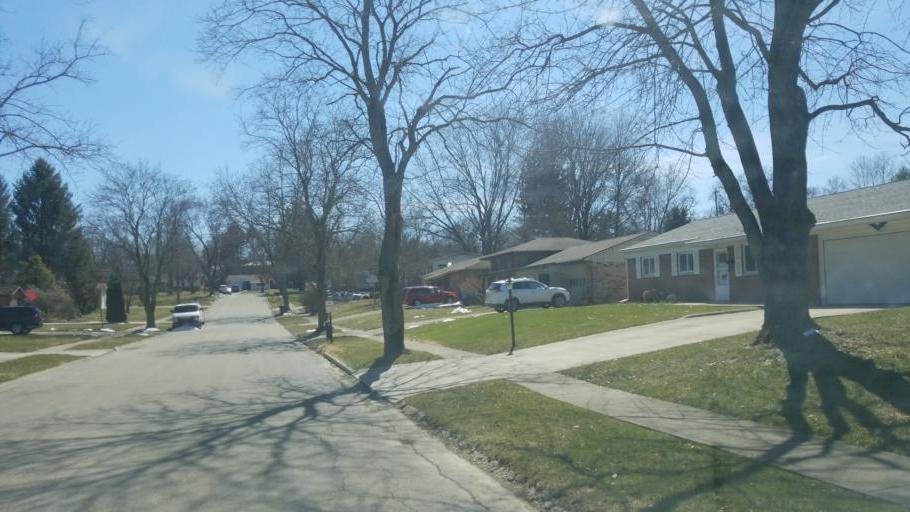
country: US
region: Ohio
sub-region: Richland County
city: Lexington
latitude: 40.6812
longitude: -82.5876
